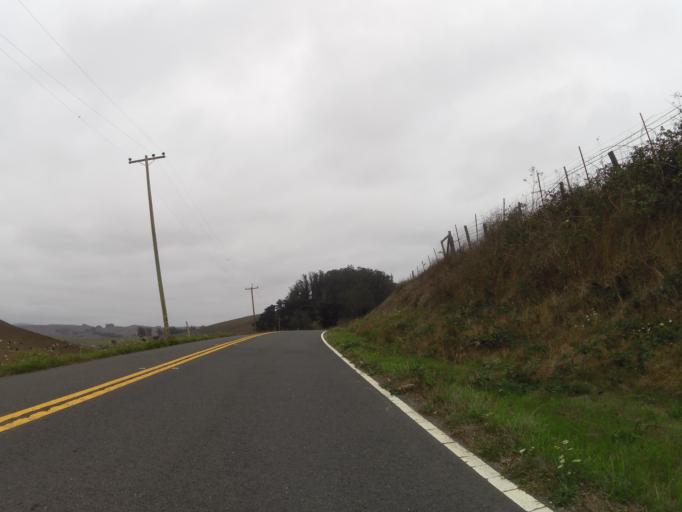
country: US
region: California
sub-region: Sonoma County
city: Occidental
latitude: 38.2948
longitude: -122.8966
